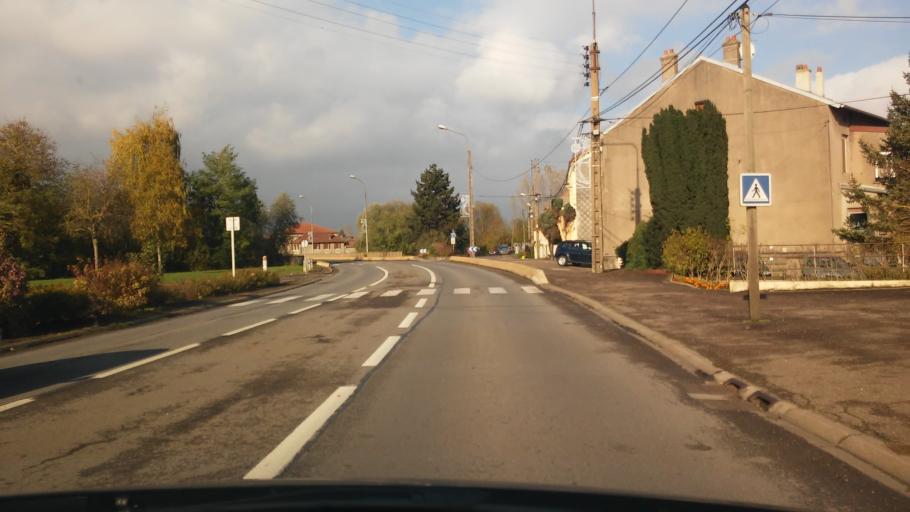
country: FR
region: Lorraine
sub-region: Departement de la Moselle
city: Richemont
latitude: 49.2763
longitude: 6.1707
